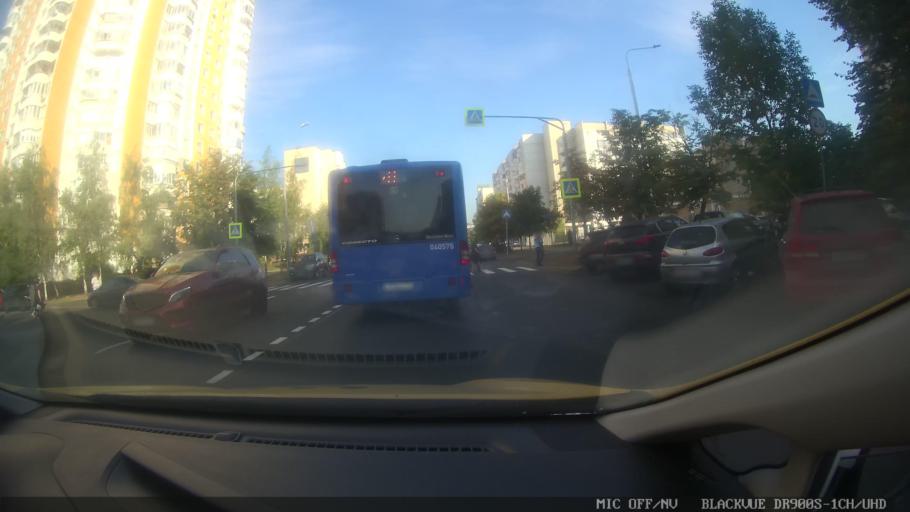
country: RU
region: Moscow
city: Zhulebino
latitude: 55.6812
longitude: 37.8569
